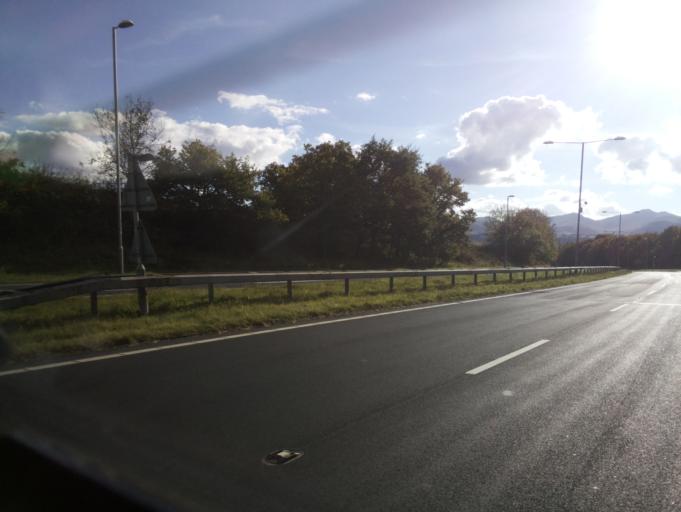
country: GB
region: Wales
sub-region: Sir Powys
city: Brecon
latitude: 51.9648
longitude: -3.3523
